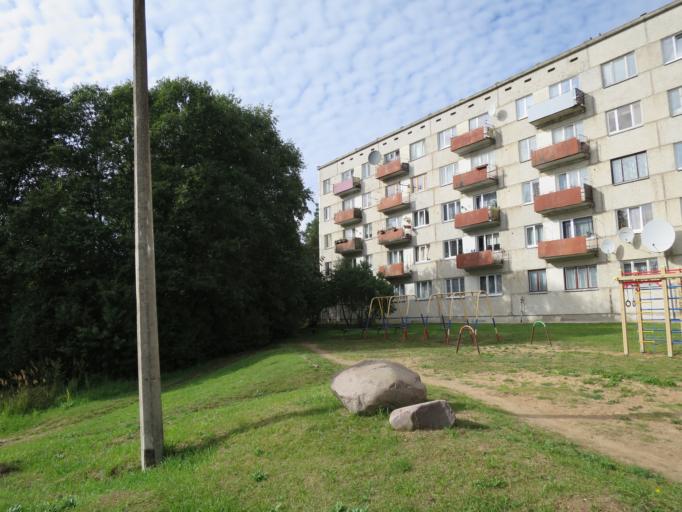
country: LV
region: Incukalns
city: Vangazi
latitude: 57.0960
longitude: 24.5425
